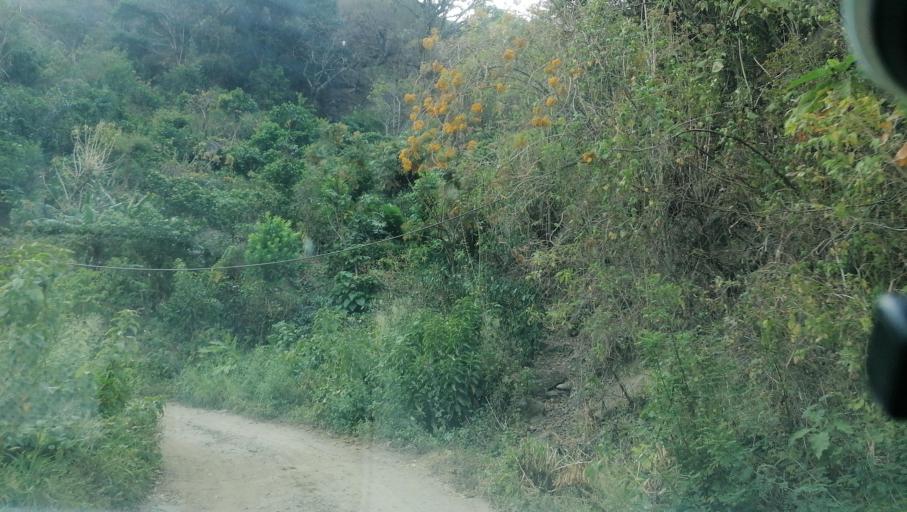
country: MX
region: Chiapas
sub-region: Cacahoatan
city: Benito Juarez
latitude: 15.1472
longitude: -92.1861
